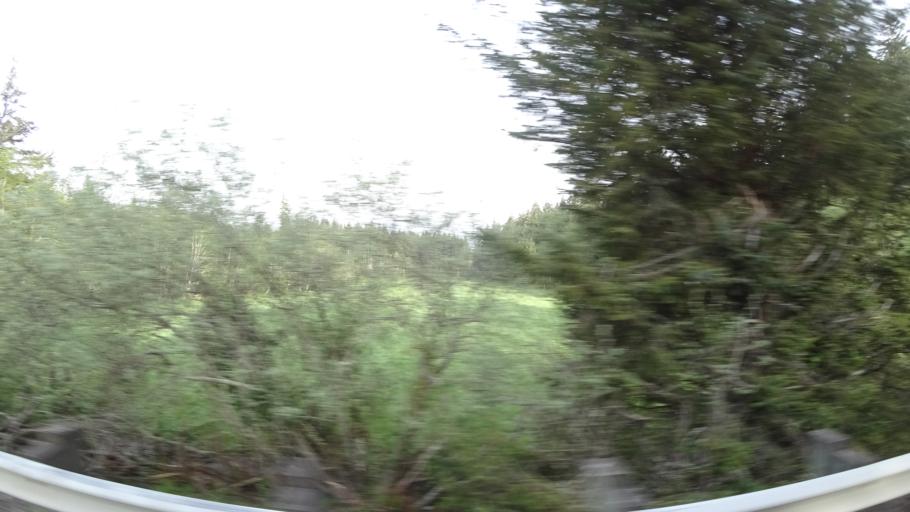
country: US
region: Oregon
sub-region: Coos County
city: Bandon
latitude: 42.9757
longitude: -124.4250
